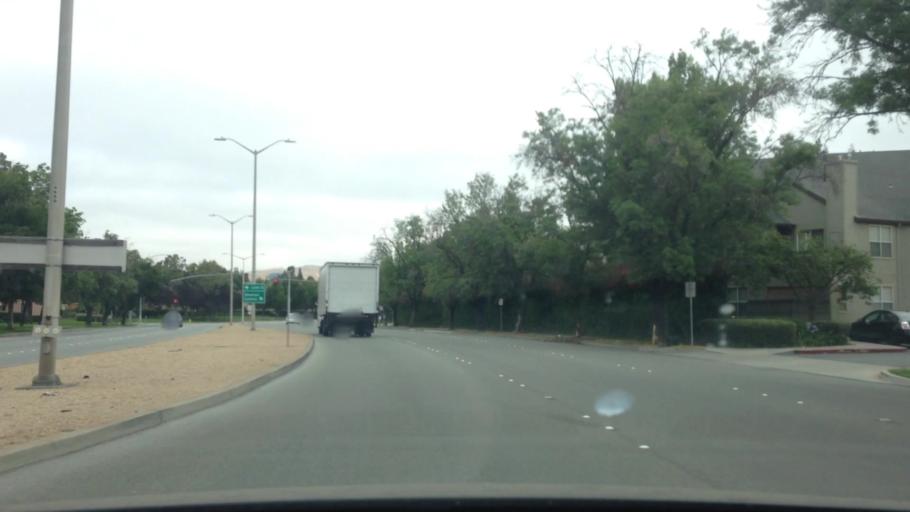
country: US
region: California
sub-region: Alameda County
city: Fremont
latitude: 37.5426
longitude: -121.9726
